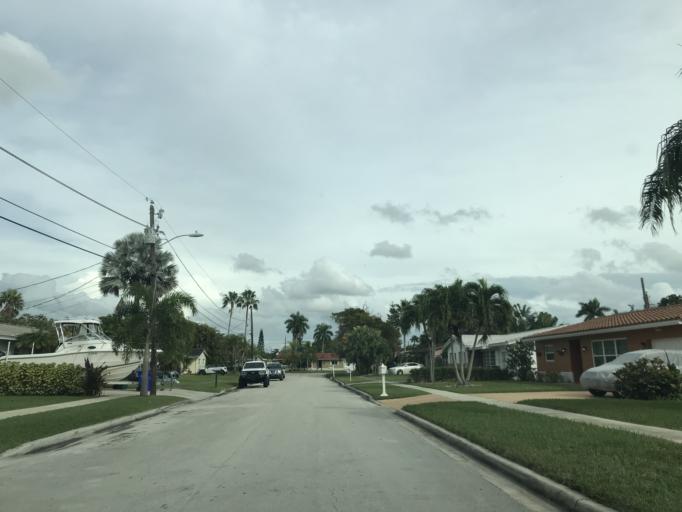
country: US
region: Florida
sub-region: Broward County
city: Margate
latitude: 26.2544
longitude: -80.2123
